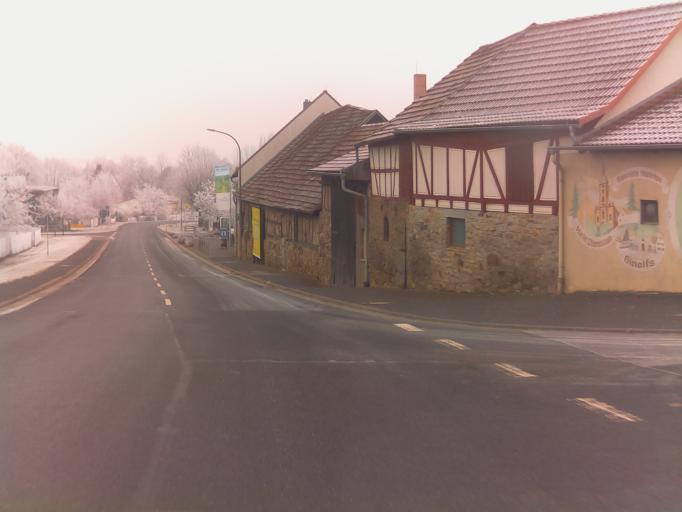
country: DE
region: Bavaria
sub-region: Regierungsbezirk Unterfranken
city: Oberelsbach
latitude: 50.4419
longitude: 10.1196
